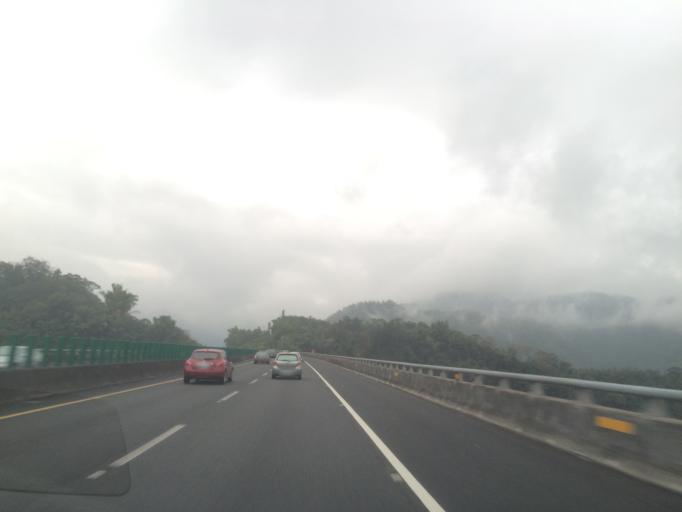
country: TW
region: Taiwan
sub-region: Nantou
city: Puli
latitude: 23.9808
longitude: 120.8925
